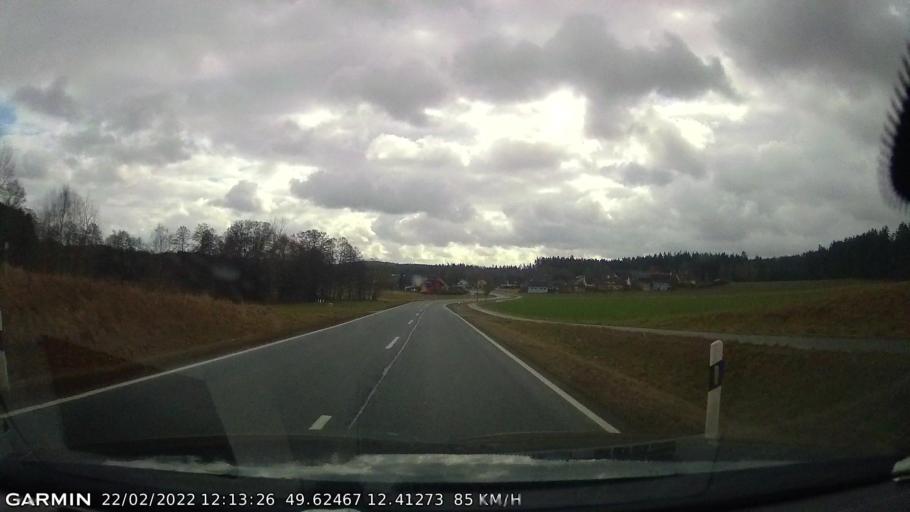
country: DE
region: Bavaria
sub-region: Upper Palatinate
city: Pleystein
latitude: 49.6244
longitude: 12.4128
